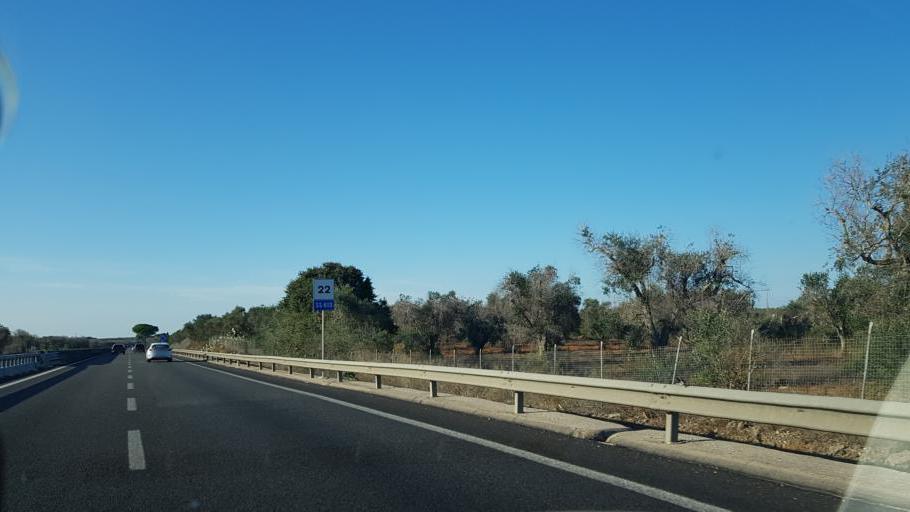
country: IT
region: Apulia
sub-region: Provincia di Lecce
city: Squinzano
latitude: 40.4480
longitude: 18.0709
